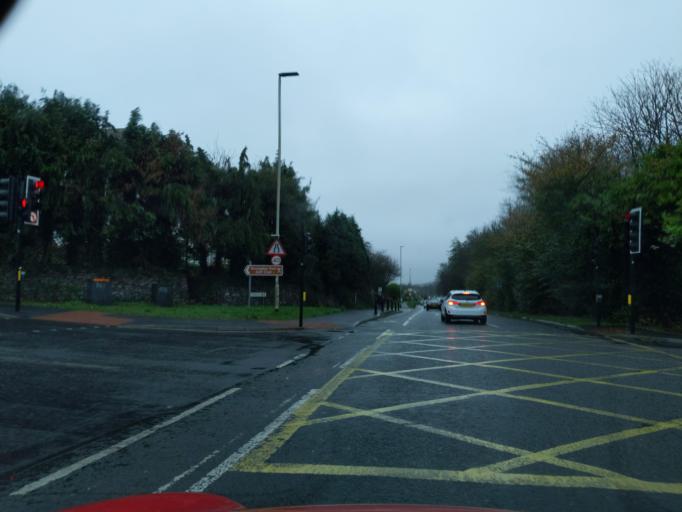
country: GB
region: England
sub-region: Devon
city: Plympton
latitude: 50.3907
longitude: -4.0710
